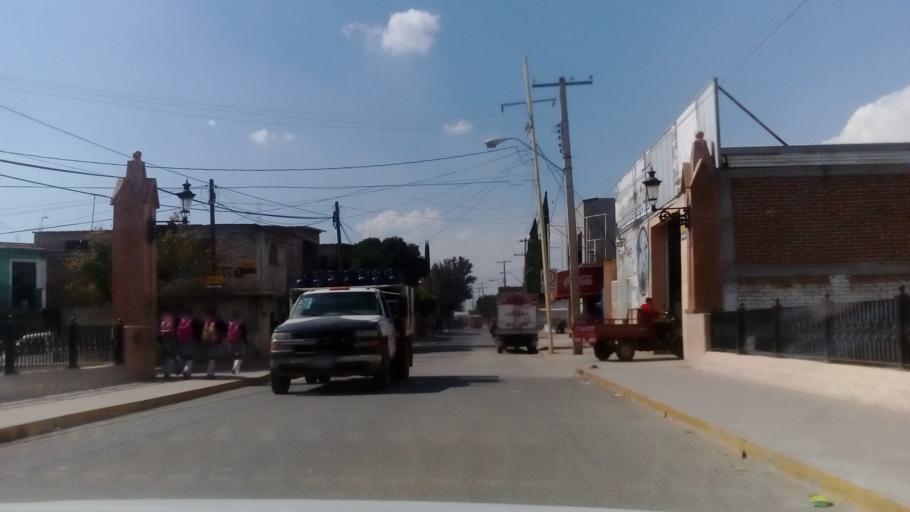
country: MX
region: Guanajuato
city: Duarte
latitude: 21.0874
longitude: -101.5246
